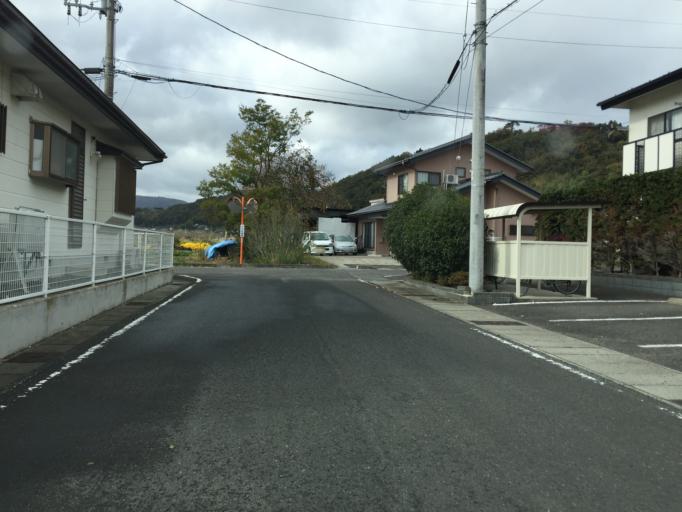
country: JP
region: Fukushima
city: Fukushima-shi
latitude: 37.8278
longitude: 140.4441
